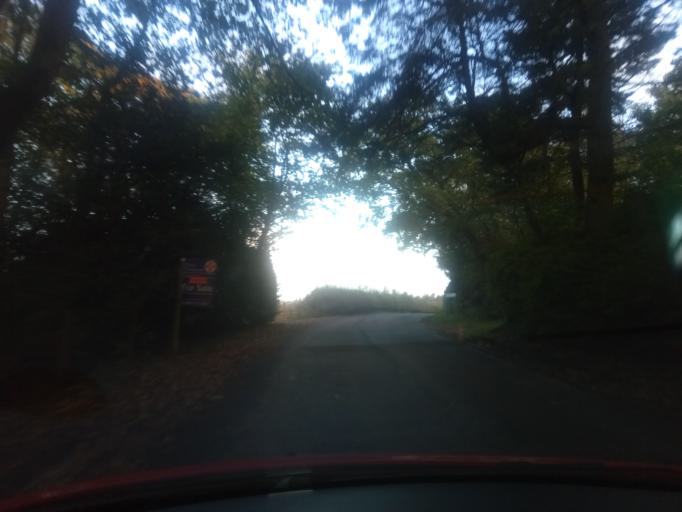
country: GB
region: Scotland
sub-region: The Scottish Borders
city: Jedburgh
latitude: 55.3841
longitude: -2.6425
